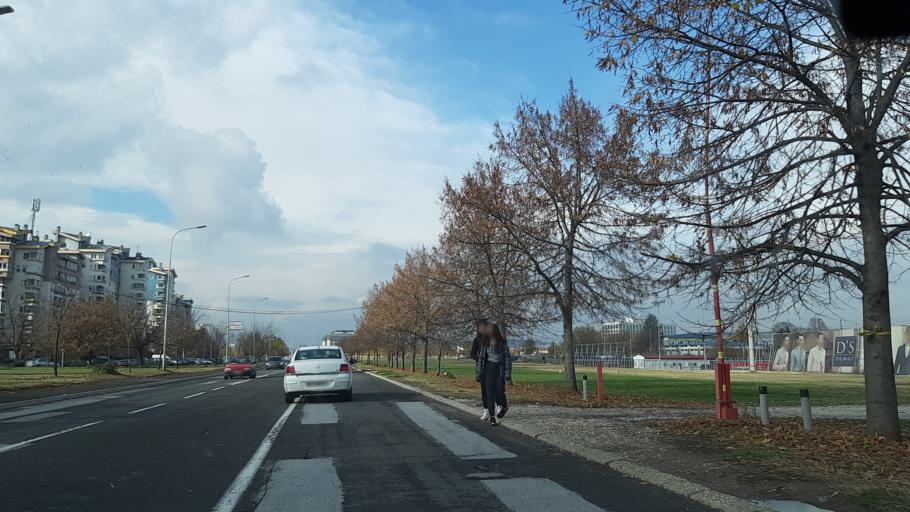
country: MK
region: Kisela Voda
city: Usje
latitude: 41.9869
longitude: 21.4802
